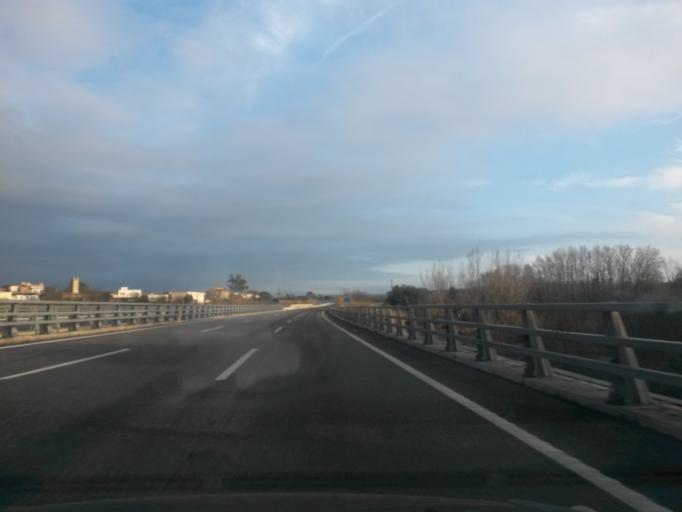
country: ES
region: Catalonia
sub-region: Provincia de Girona
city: Vilafant
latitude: 42.2428
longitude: 2.9386
